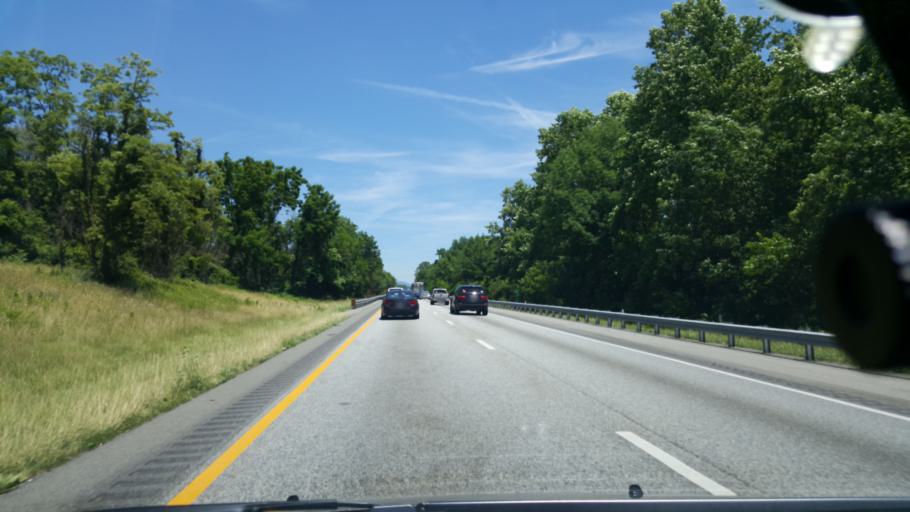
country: US
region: Virginia
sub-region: Botetourt County
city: Daleville
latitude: 37.4320
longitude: -79.8731
